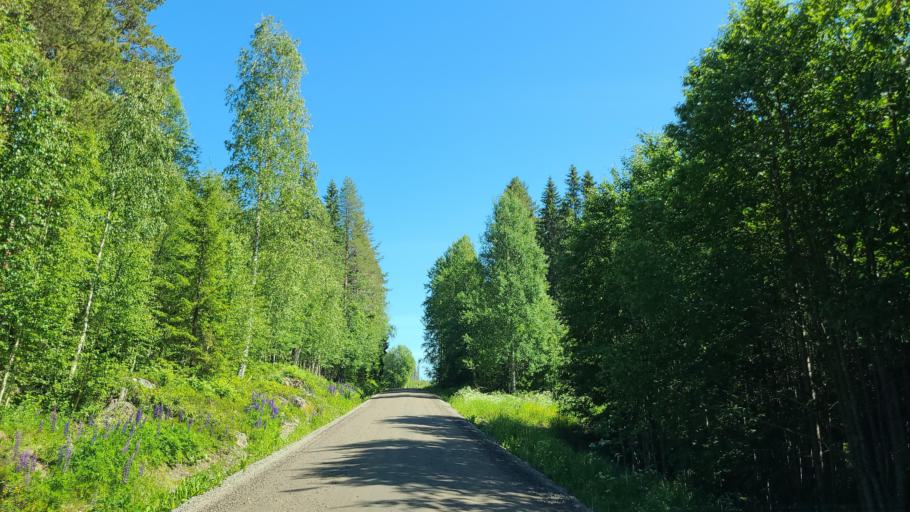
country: SE
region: Vaesterbotten
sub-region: Bjurholms Kommun
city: Bjurholm
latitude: 63.6760
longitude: 19.0485
